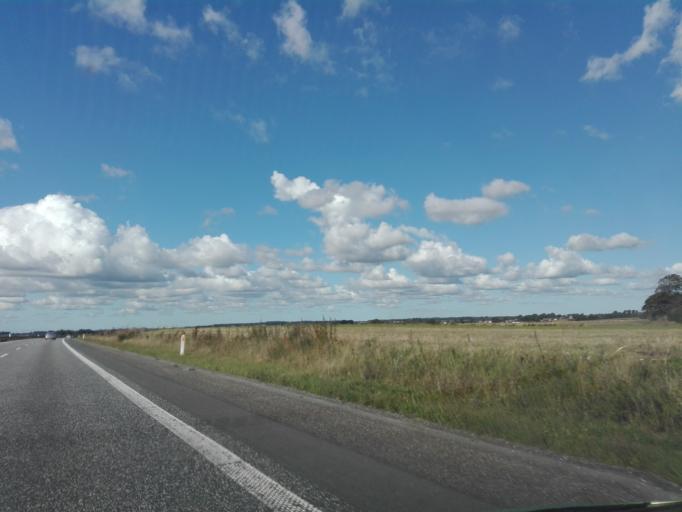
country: DK
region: Central Jutland
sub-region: Randers Kommune
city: Spentrup
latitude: 56.5299
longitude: 9.9331
